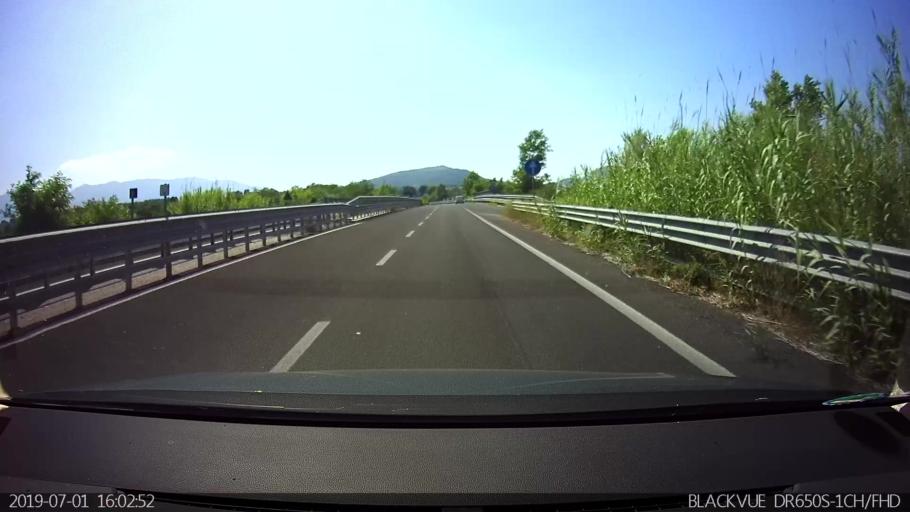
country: IT
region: Latium
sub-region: Provincia di Frosinone
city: Tecchiena
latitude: 41.6728
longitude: 13.3462
